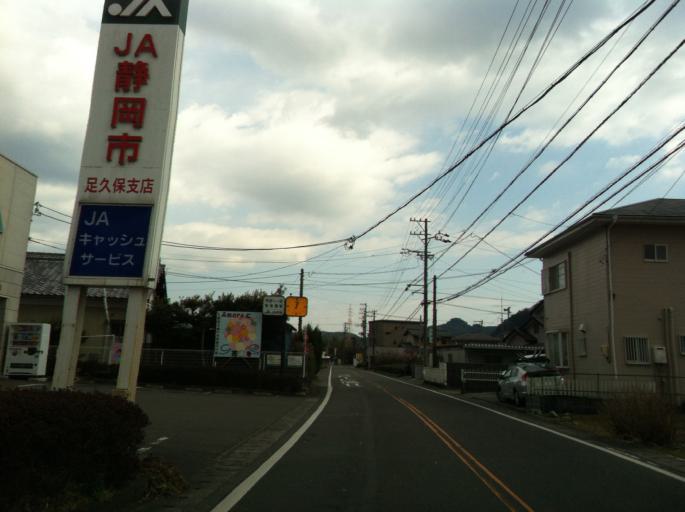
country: JP
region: Shizuoka
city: Shizuoka-shi
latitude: 35.0454
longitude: 138.3593
